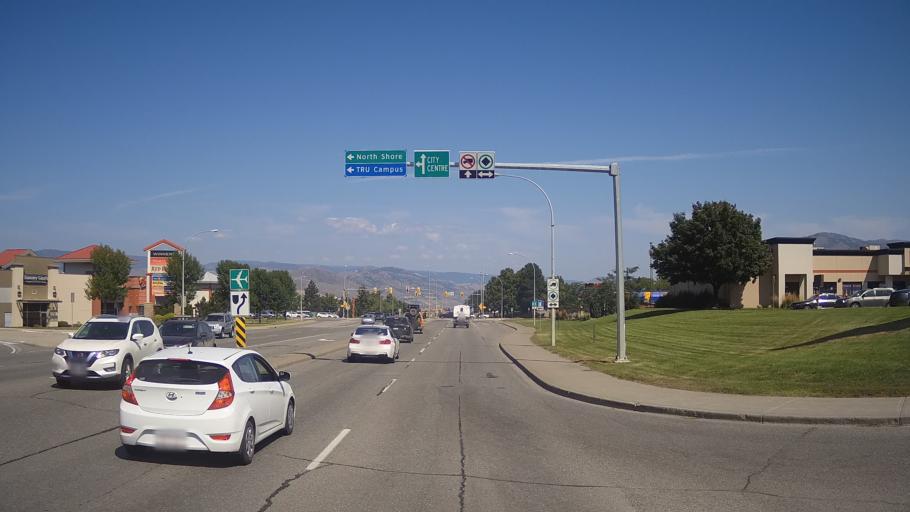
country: CA
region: British Columbia
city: Kamloops
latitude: 50.6652
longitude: -120.3539
